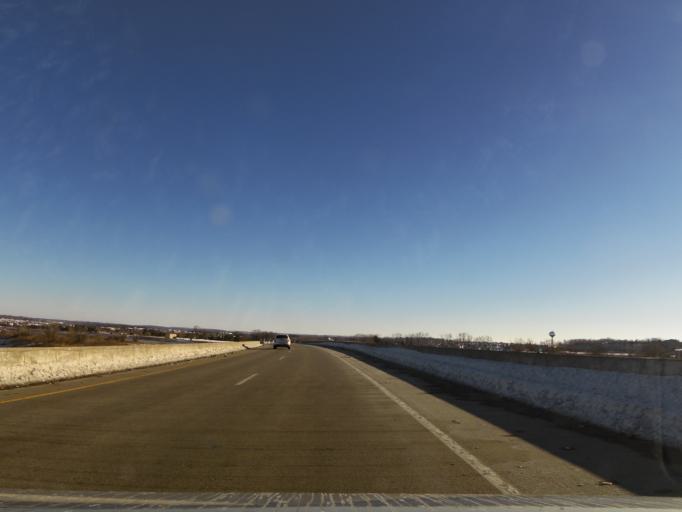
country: US
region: Wisconsin
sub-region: Dane County
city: Monona
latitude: 43.1046
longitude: -89.2826
